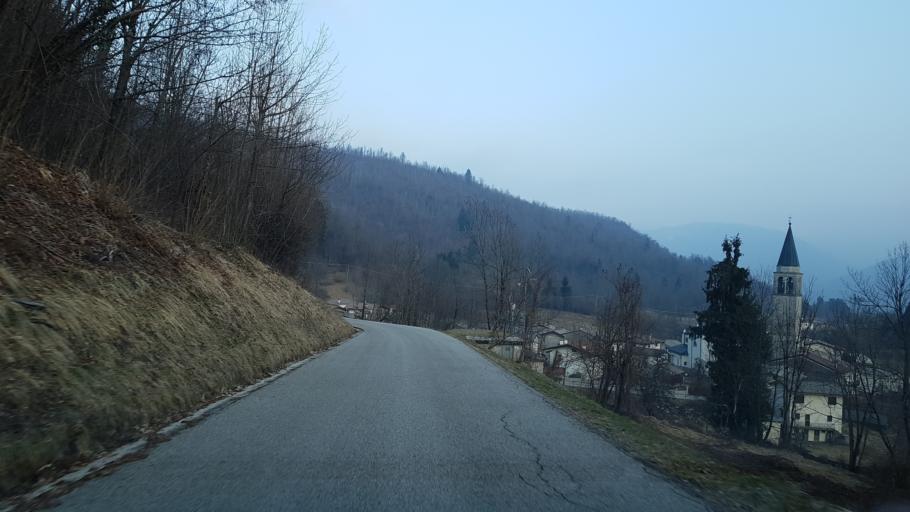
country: IT
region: Friuli Venezia Giulia
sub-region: Provincia di Udine
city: Taipana
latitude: 46.2427
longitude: 13.3794
